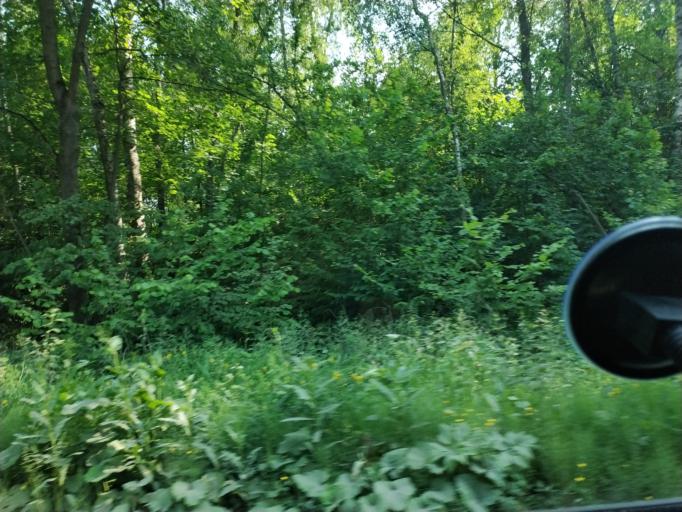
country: RU
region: Moskovskaya
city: Yakovlevskoye
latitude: 55.4315
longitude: 37.9236
